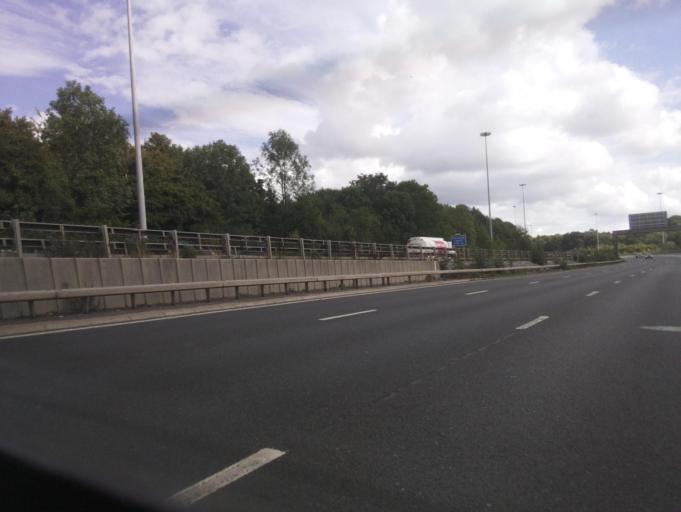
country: GB
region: England
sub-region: Borough of Stockport
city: Bredbury
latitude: 53.4206
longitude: -2.1363
